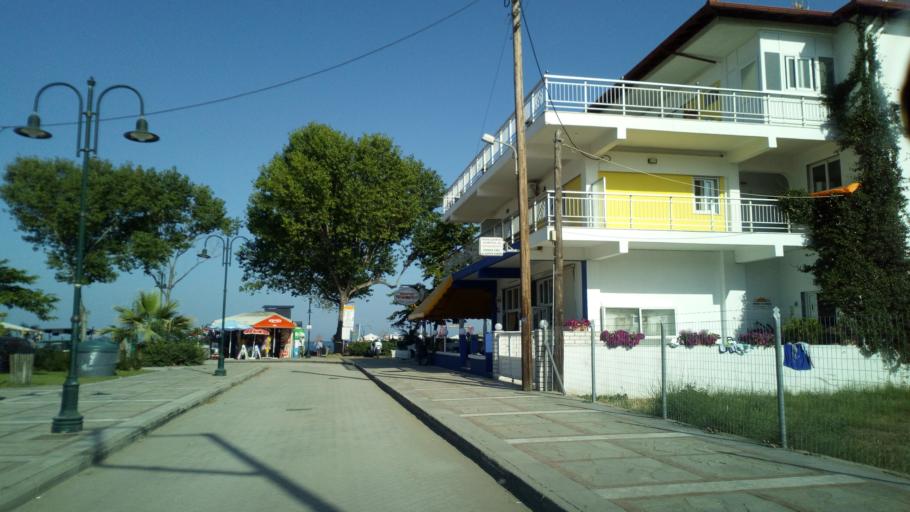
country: GR
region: Central Macedonia
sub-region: Nomos Thessalonikis
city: Nea Vrasna
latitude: 40.7074
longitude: 23.7016
